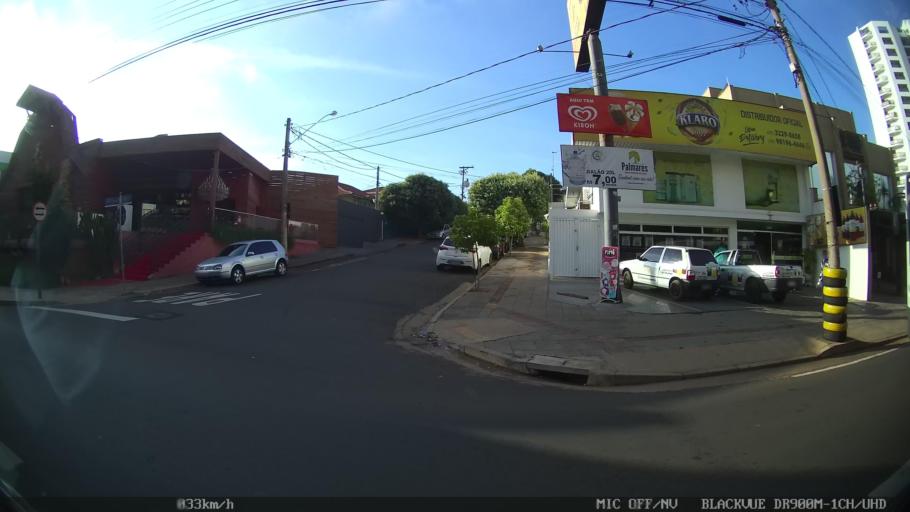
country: BR
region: Sao Paulo
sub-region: Sao Jose Do Rio Preto
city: Sao Jose do Rio Preto
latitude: -20.8203
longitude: -49.3831
